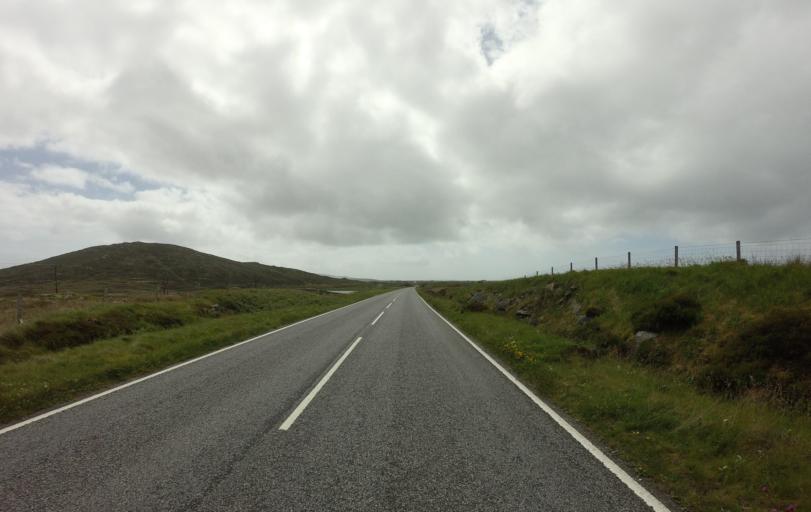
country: GB
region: Scotland
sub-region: Eilean Siar
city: Isle of South Uist
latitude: 57.1954
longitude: -7.3894
